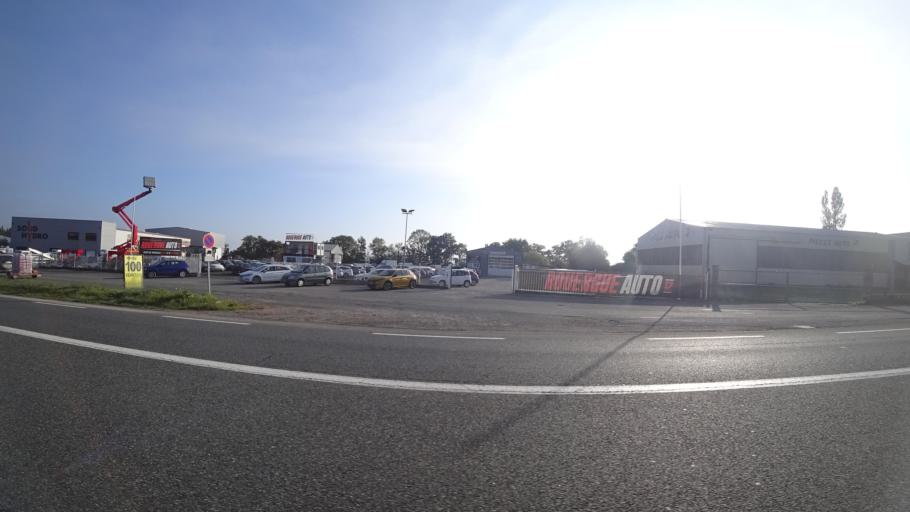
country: FR
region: Midi-Pyrenees
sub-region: Departement de l'Aveyron
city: Luc-la-Primaube
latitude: 44.3177
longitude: 2.5581
